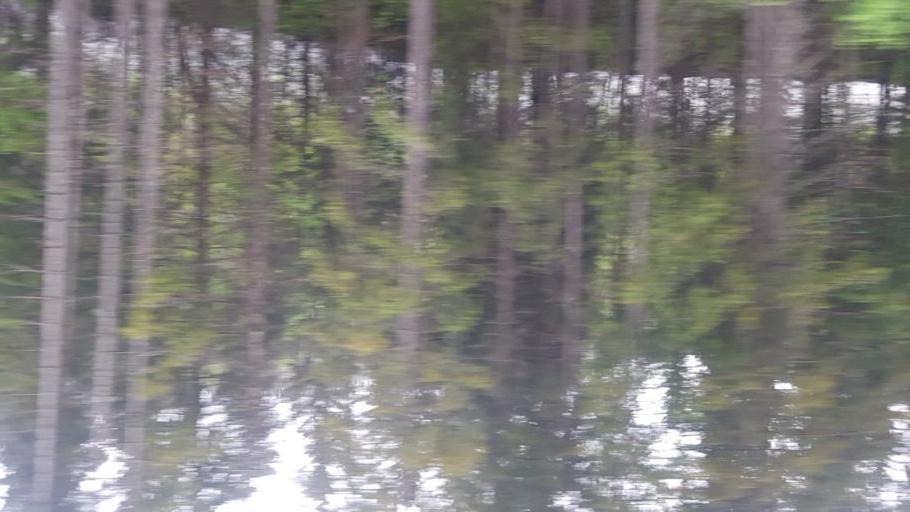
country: NO
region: Oppland
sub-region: Oyer
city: Tretten
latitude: 61.2726
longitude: 10.3772
